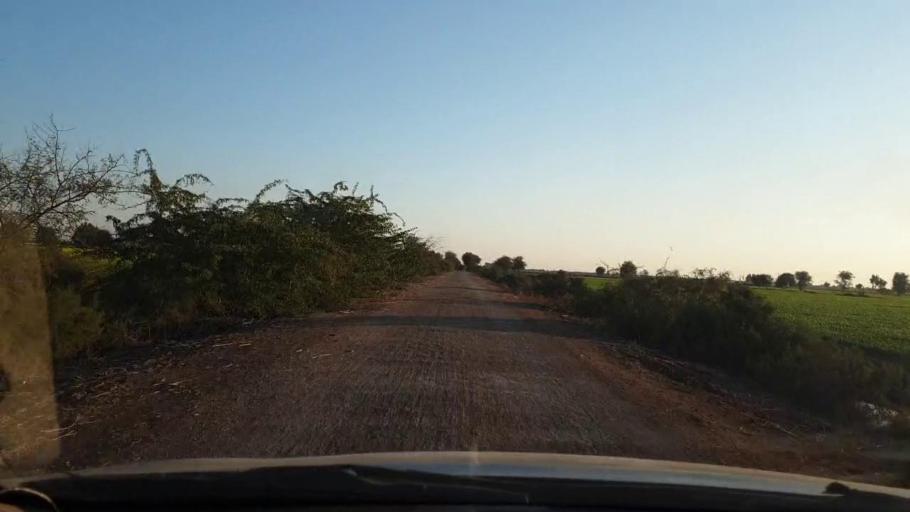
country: PK
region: Sindh
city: Jhol
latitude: 25.8804
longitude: 68.8953
